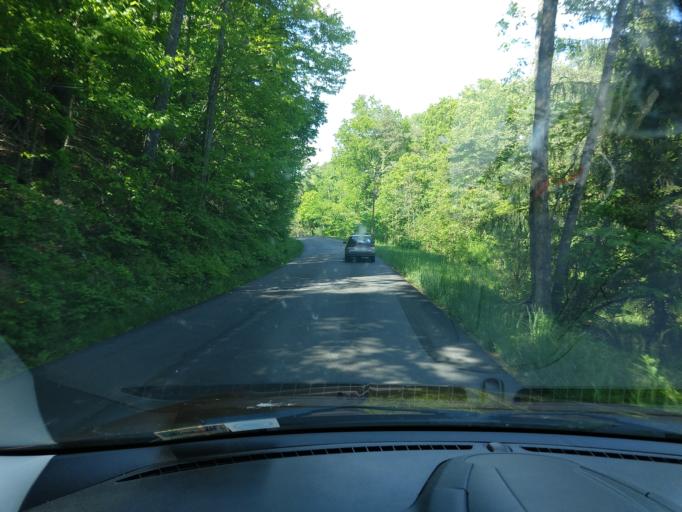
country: US
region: Virginia
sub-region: City of Covington
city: Fairlawn
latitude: 37.6981
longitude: -79.8877
